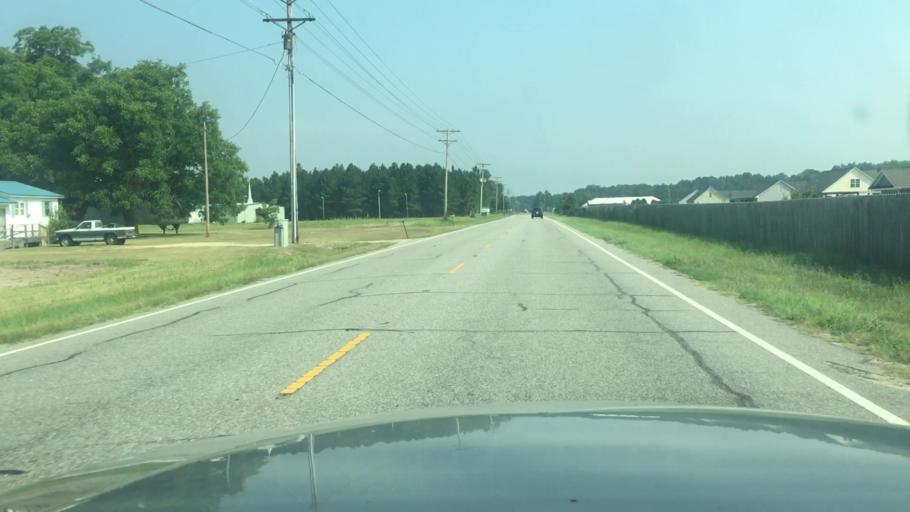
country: US
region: North Carolina
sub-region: Cumberland County
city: Hope Mills
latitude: 34.9012
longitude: -78.9010
